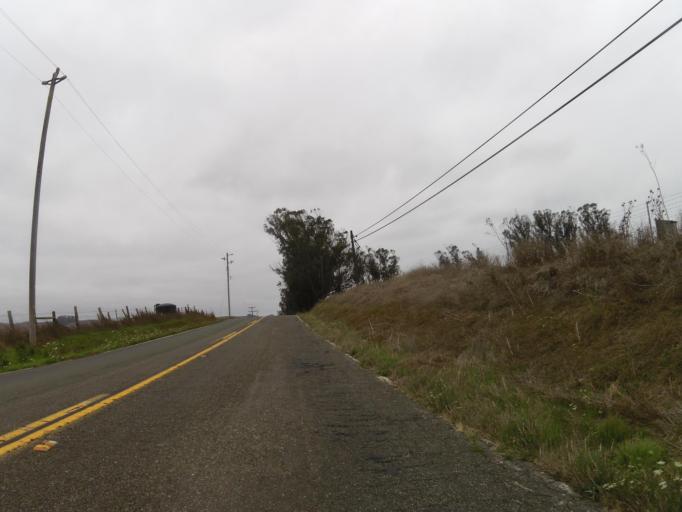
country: US
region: California
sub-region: Sonoma County
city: Occidental
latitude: 38.2821
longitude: -122.9001
